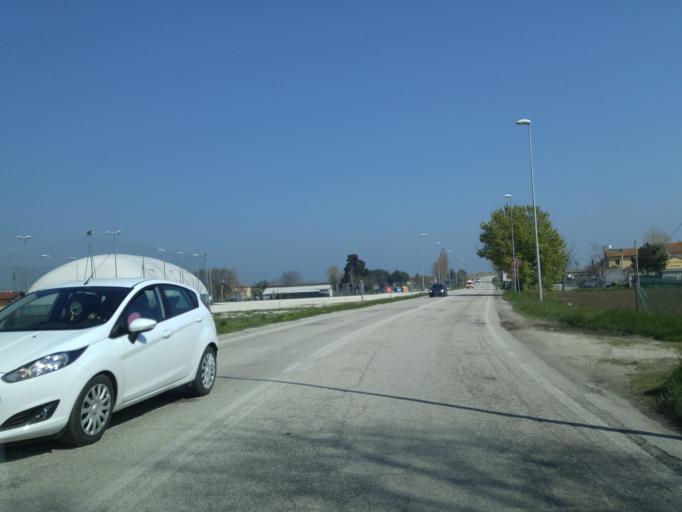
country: IT
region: The Marches
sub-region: Provincia di Pesaro e Urbino
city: Rosciano
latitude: 43.8101
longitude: 13.0144
